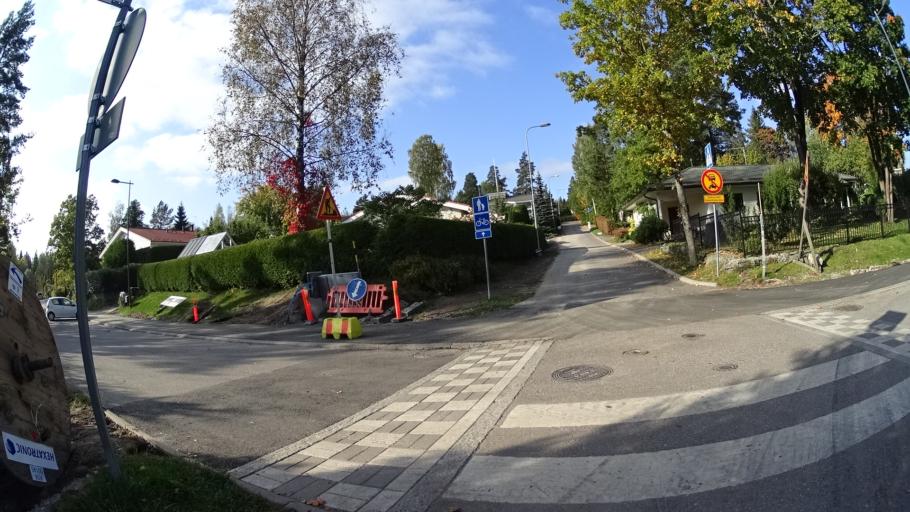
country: FI
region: Uusimaa
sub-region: Helsinki
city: Kilo
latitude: 60.2349
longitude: 24.8042
